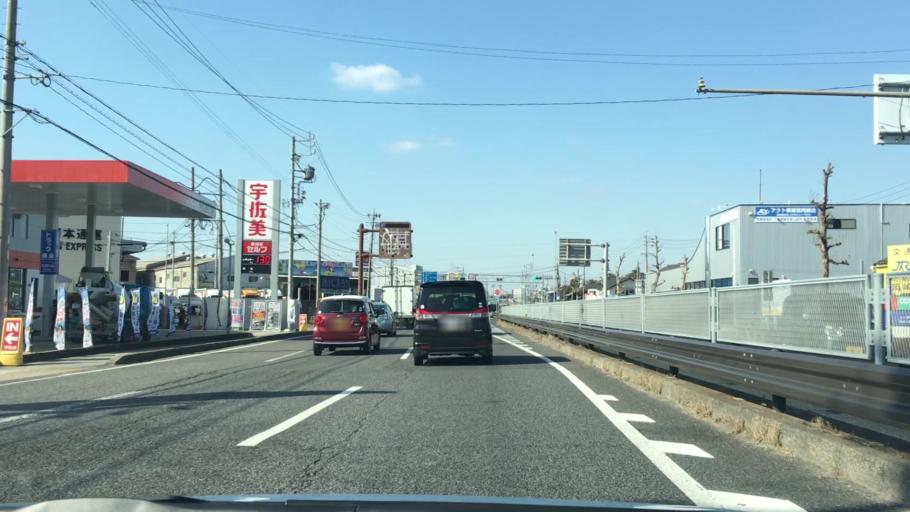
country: JP
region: Aichi
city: Okazaki
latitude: 34.9477
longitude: 137.1859
